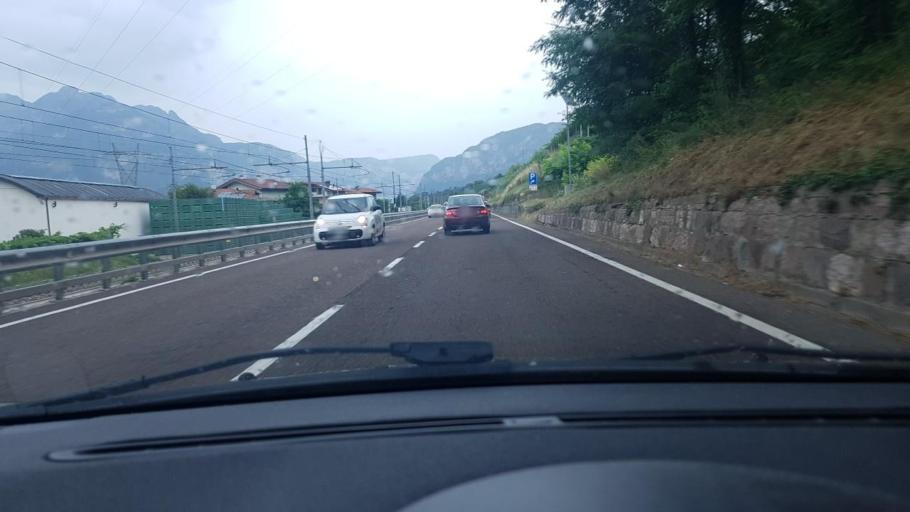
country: IT
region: Trentino-Alto Adige
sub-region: Provincia di Trento
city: Nave San Rocco
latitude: 46.1603
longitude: 11.1080
